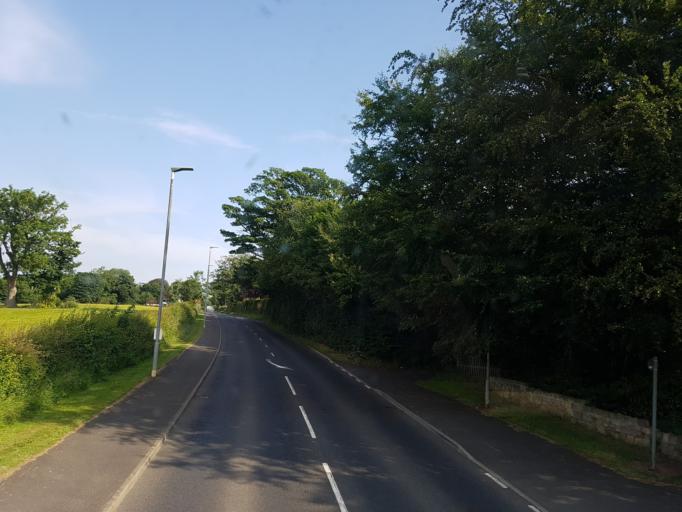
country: GB
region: England
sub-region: Northumberland
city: Alnmouth
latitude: 55.3993
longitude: -1.6353
